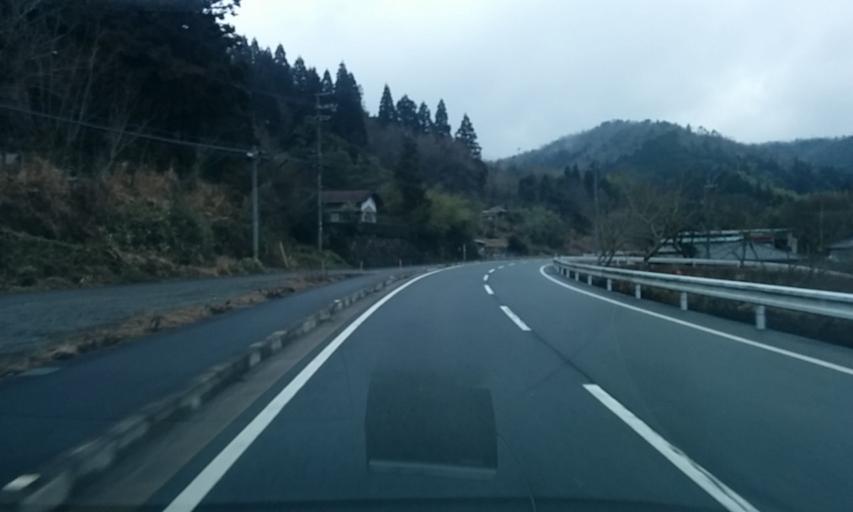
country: JP
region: Kyoto
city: Ayabe
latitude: 35.2461
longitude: 135.2658
